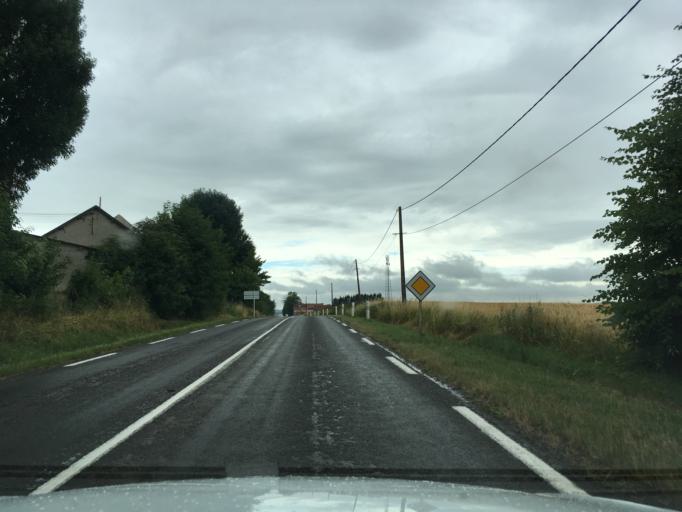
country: FR
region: Picardie
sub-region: Departement de l'Aisne
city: Guise
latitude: 49.8693
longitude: 3.5654
